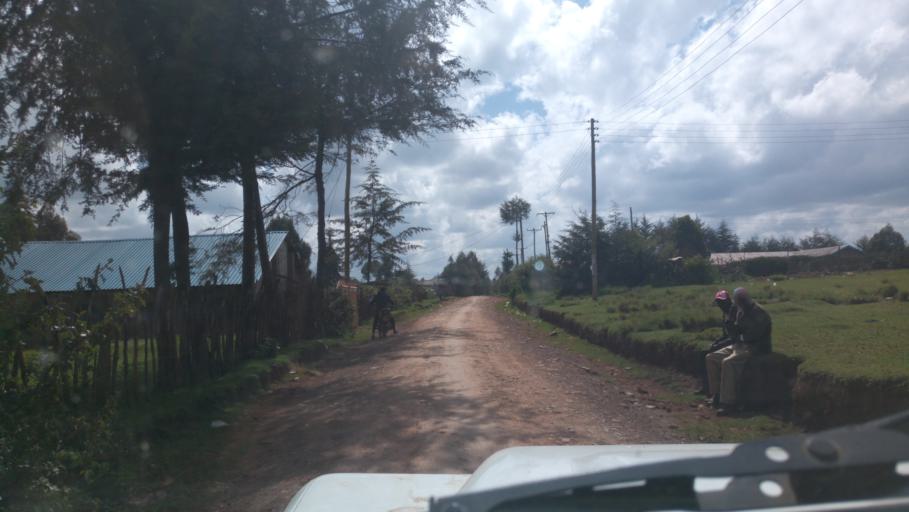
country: KE
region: Nakuru
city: Molo
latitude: -0.4778
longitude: 35.6791
